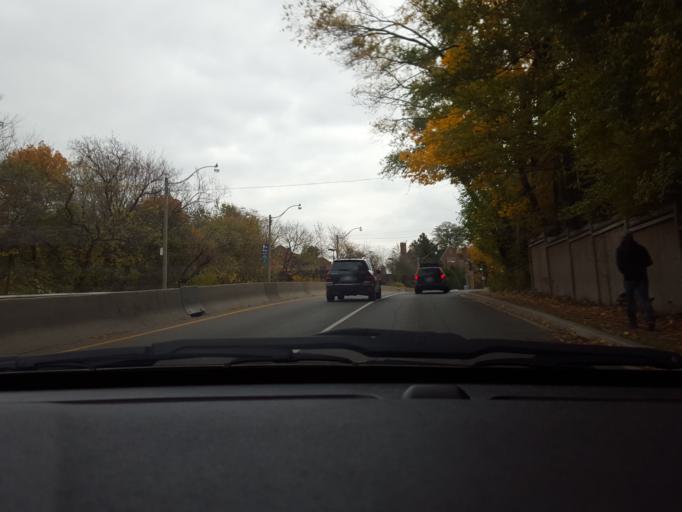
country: CA
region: Ontario
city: Toronto
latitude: 43.6800
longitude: -79.3819
